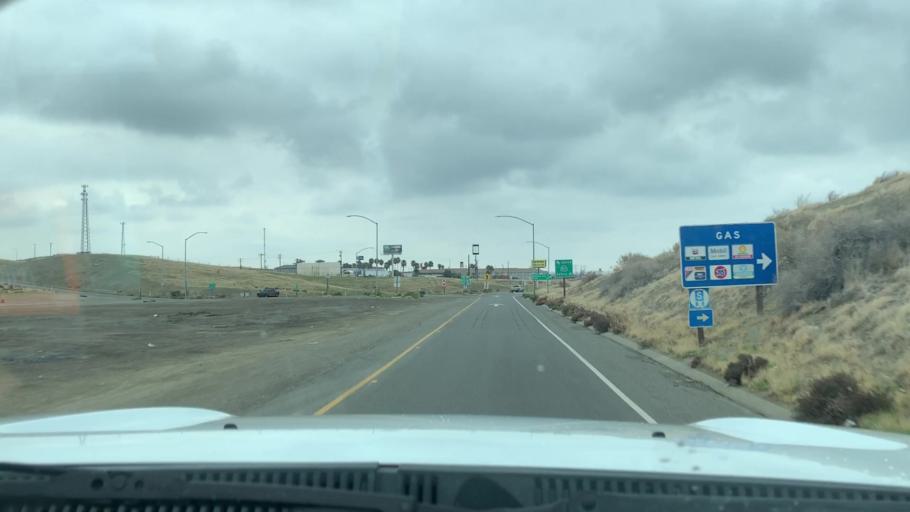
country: US
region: California
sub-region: Kings County
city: Kettleman City
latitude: 35.9827
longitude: -119.9591
